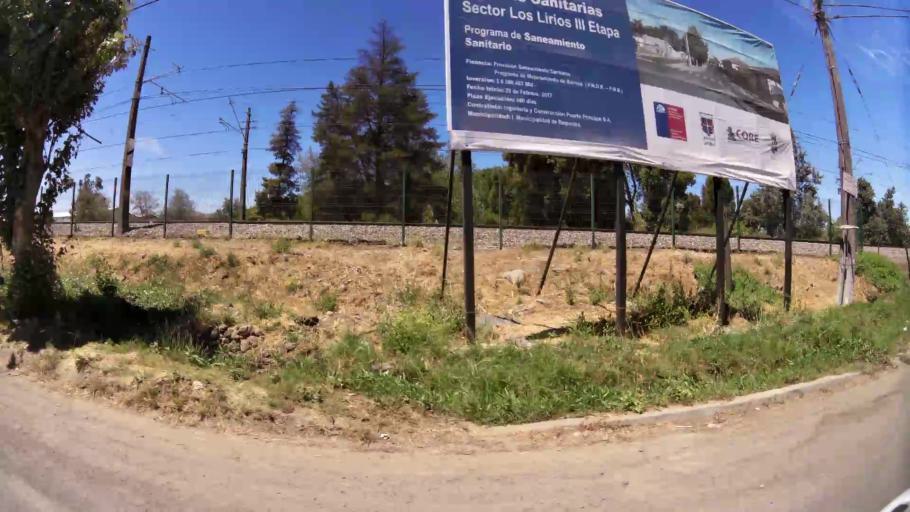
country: CL
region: O'Higgins
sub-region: Provincia de Cachapoal
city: Rancagua
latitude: -34.2240
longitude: -70.7833
